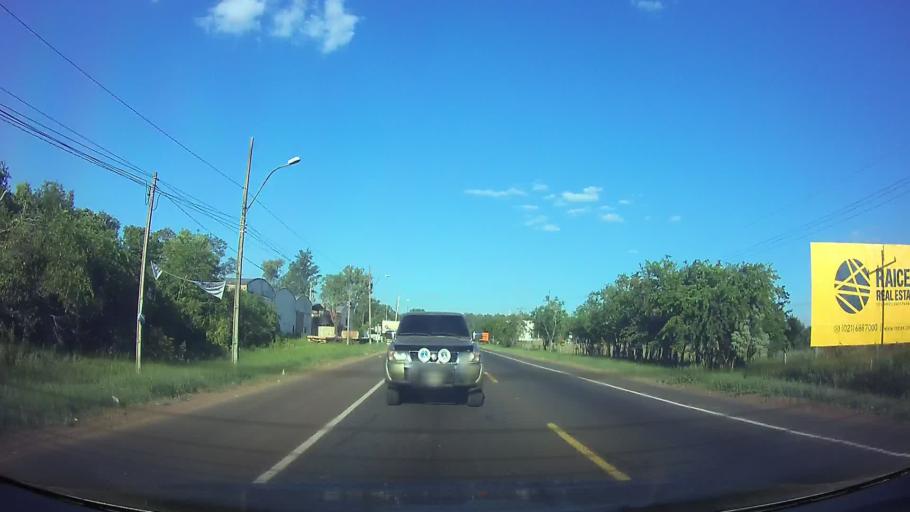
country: PY
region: Central
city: Ypacarai
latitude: -25.3779
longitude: -57.2380
